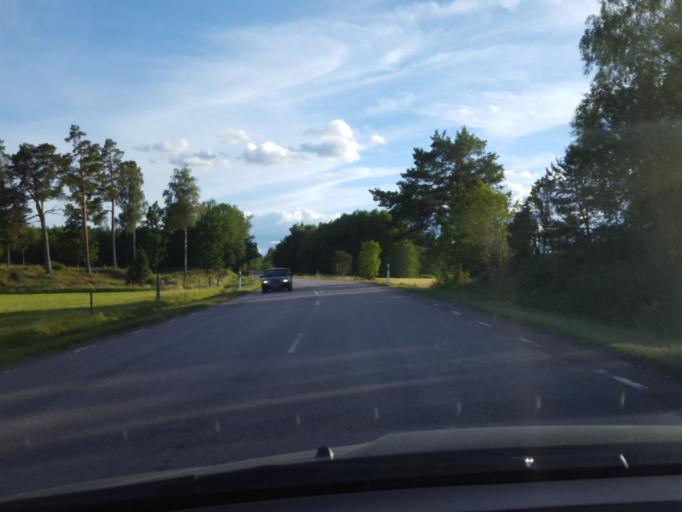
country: SE
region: Uppsala
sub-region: Osthammars Kommun
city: Gimo
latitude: 60.2188
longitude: 18.2162
